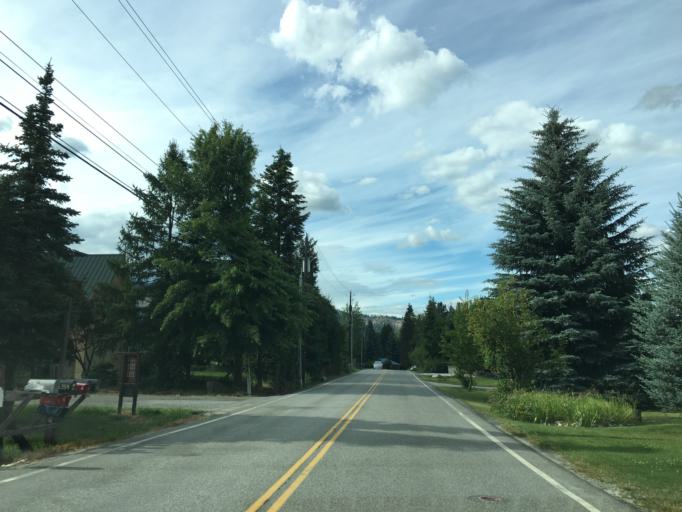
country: US
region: Washington
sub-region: Chelan County
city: Leavenworth
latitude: 47.5871
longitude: -120.6597
